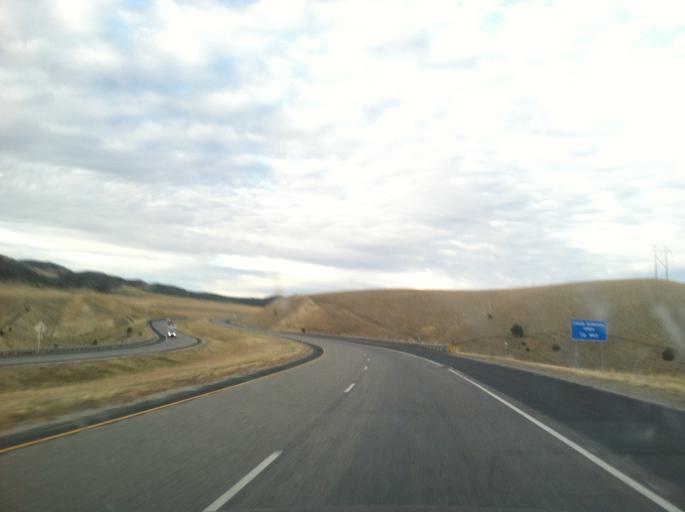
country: US
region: Montana
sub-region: Jefferson County
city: Whitehall
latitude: 45.8786
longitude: -111.8811
